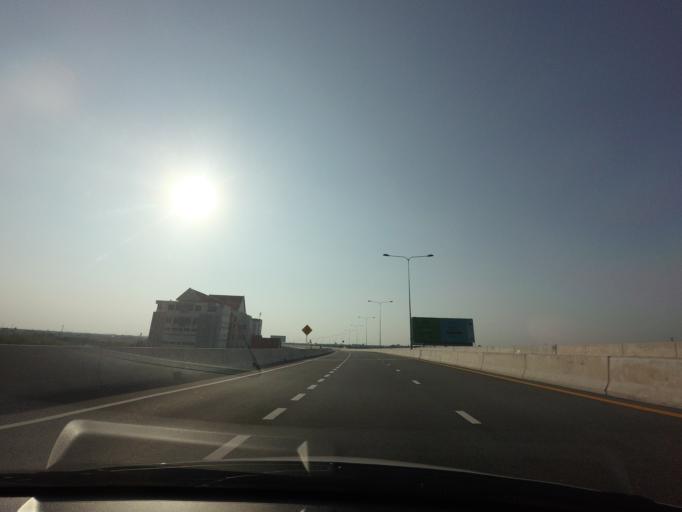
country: TH
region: Bangkok
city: Taling Chan
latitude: 13.7970
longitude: 100.4307
